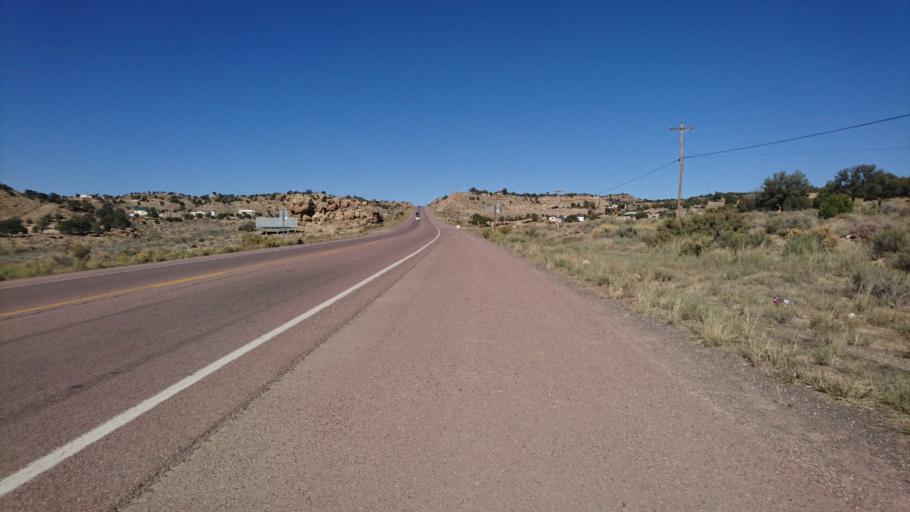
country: US
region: New Mexico
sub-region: McKinley County
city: Gallup
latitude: 35.4685
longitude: -108.7425
